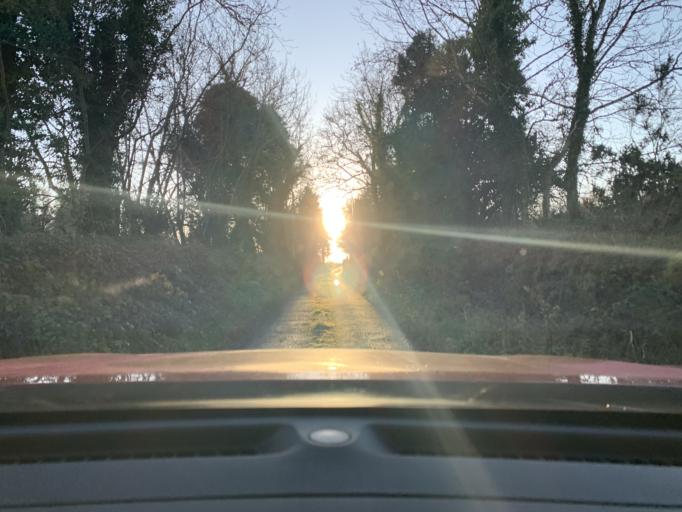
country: IE
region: Connaught
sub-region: Sligo
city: Ballymote
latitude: 53.9836
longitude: -8.5122
